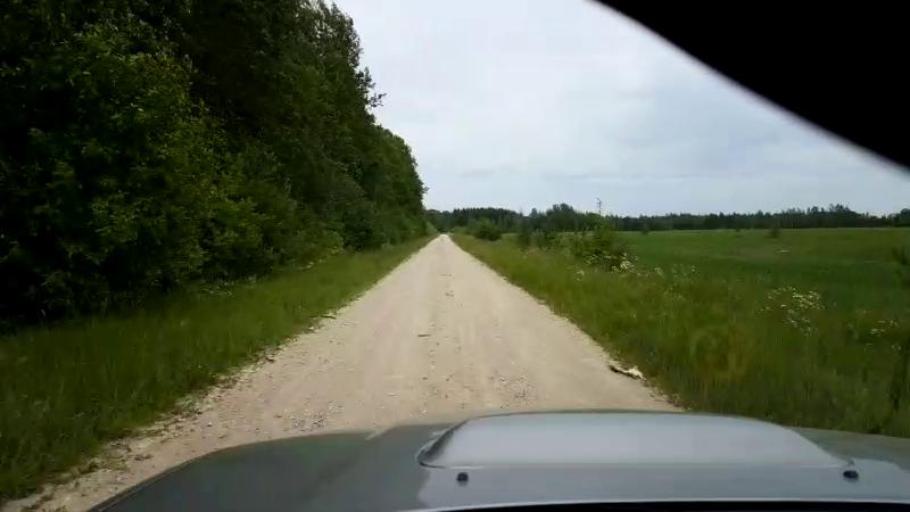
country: EE
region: Paernumaa
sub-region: Sindi linn
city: Sindi
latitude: 58.5209
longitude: 24.6211
